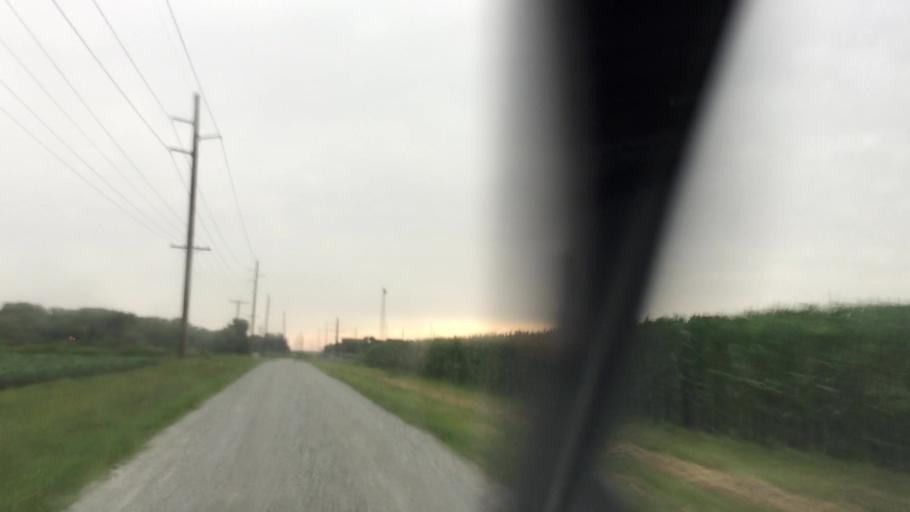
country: US
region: Iowa
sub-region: Lee County
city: Fort Madison
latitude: 40.6023
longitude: -91.2676
